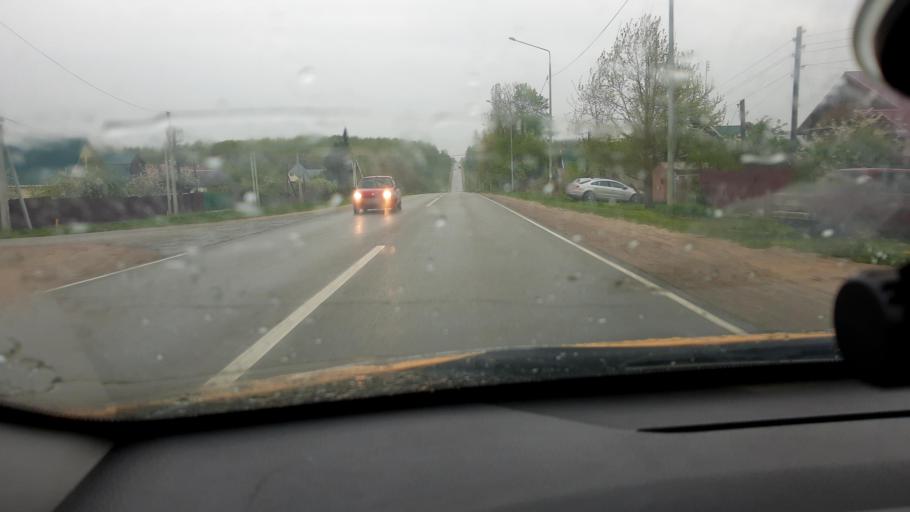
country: RU
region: Tula
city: Zaokskiy
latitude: 54.7438
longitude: 37.4395
